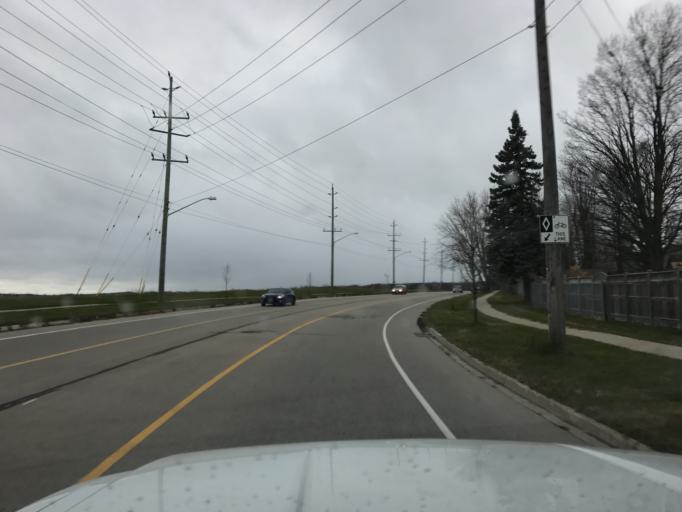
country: CA
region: Ontario
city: Waterloo
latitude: 43.4830
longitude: -80.5553
